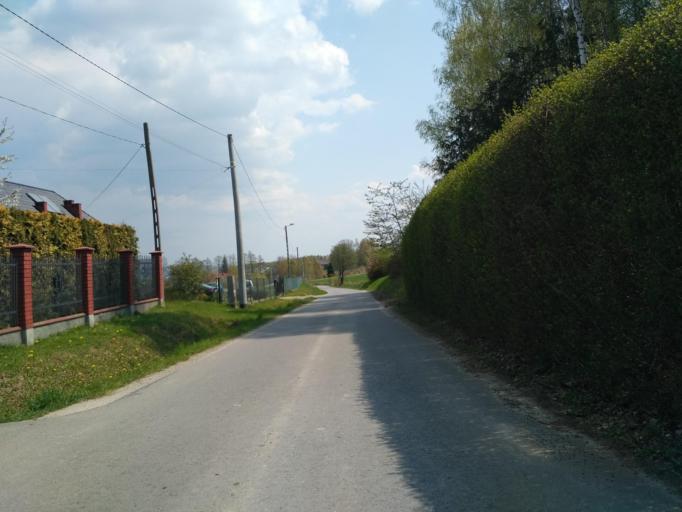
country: PL
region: Subcarpathian Voivodeship
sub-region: Powiat jasielski
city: Jaslo
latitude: 49.7178
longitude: 21.5060
